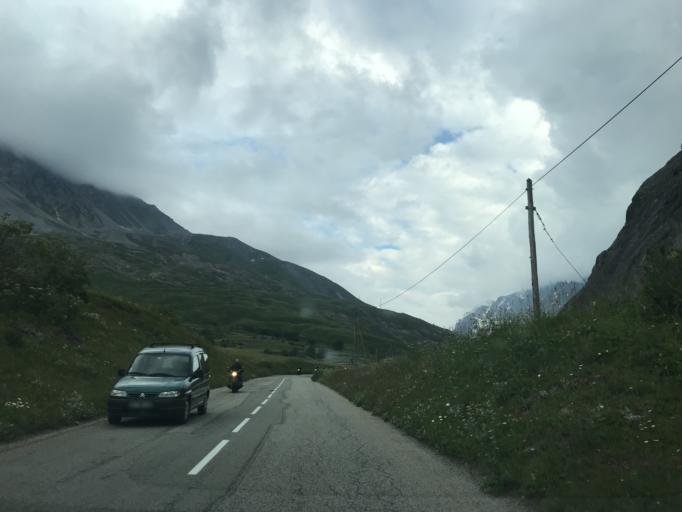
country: FR
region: Rhone-Alpes
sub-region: Departement de la Savoie
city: Valloire
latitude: 45.1173
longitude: 6.4202
